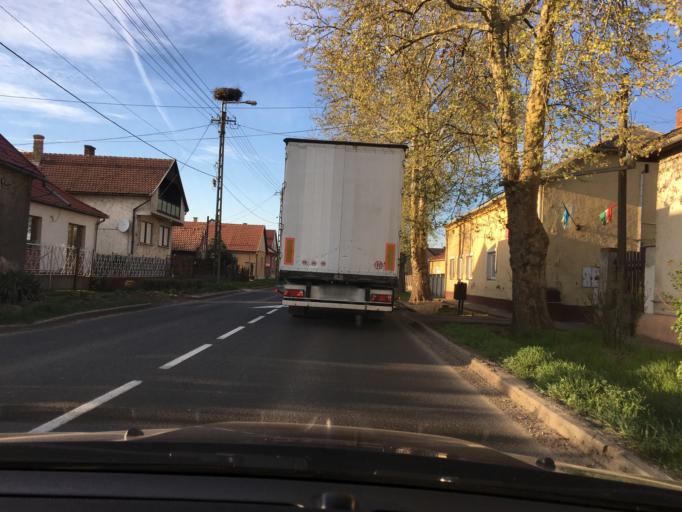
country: HU
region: Hajdu-Bihar
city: Mikepercs
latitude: 47.4437
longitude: 21.6318
